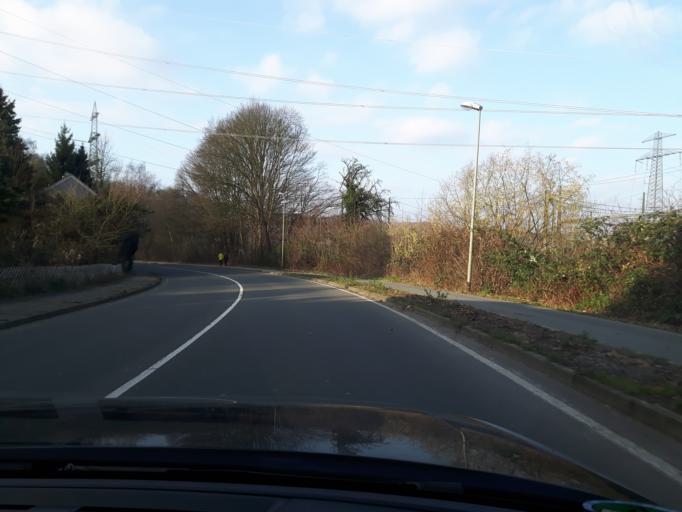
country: DE
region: North Rhine-Westphalia
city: Hattingen
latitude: 51.3886
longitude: 7.1687
